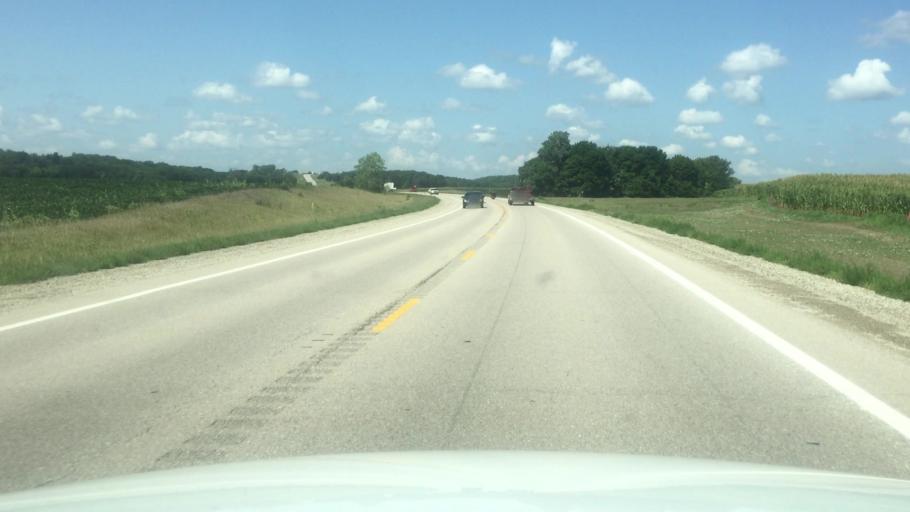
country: US
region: Kansas
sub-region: Brown County
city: Hiawatha
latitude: 39.8483
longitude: -95.6697
